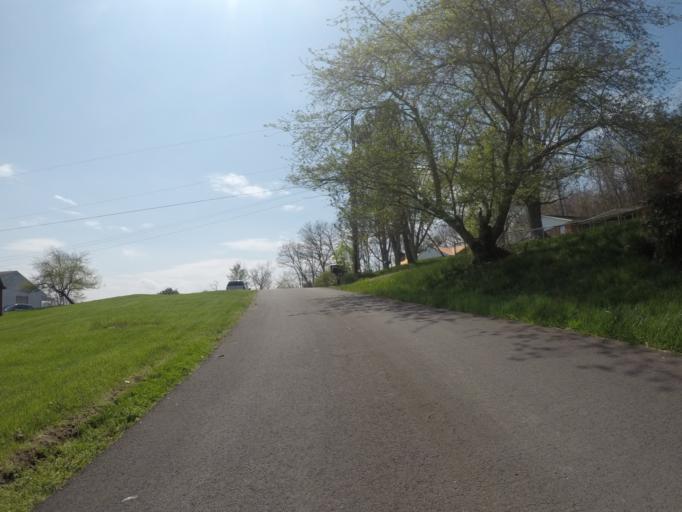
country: US
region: Ohio
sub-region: Lawrence County
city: Burlington
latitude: 38.3818
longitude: -82.5285
